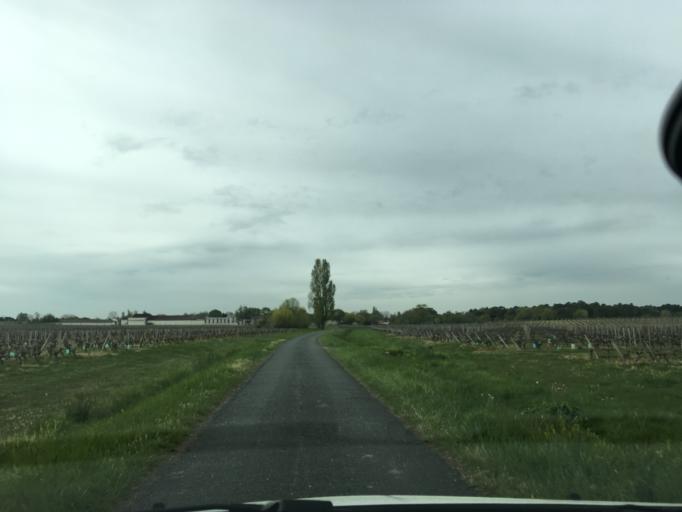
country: FR
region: Aquitaine
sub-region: Departement de la Gironde
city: Lesparre-Medoc
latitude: 45.3184
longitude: -0.8951
